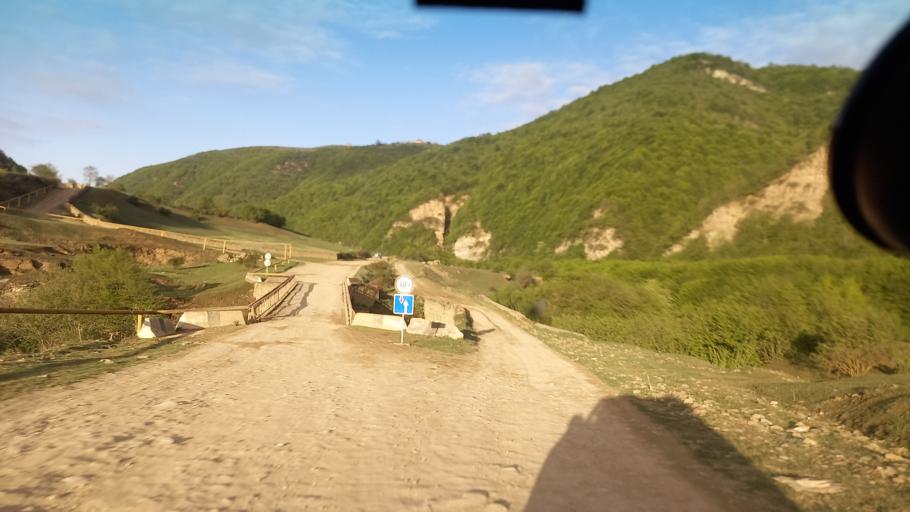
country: RU
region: Dagestan
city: Khuchni
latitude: 41.9614
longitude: 47.8644
